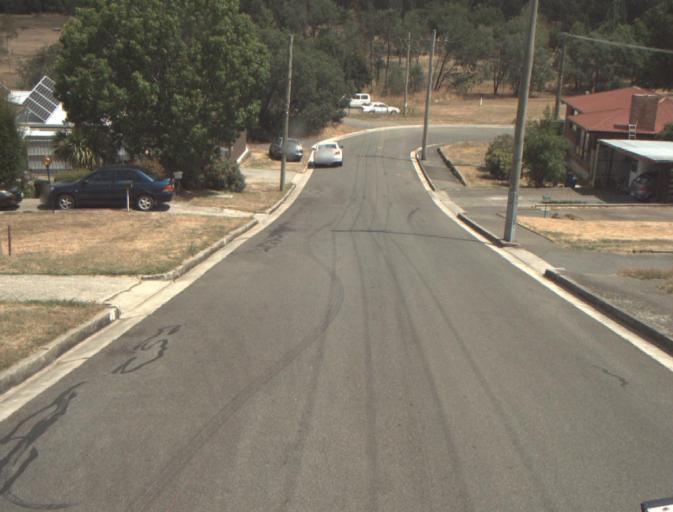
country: AU
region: Tasmania
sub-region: Launceston
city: Newnham
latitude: -41.4095
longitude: 147.1446
